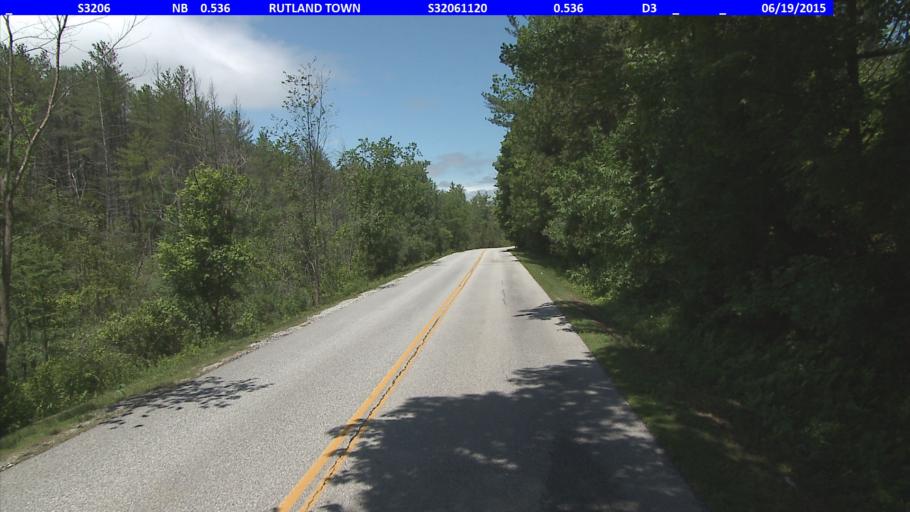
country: US
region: Vermont
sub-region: Rutland County
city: Rutland
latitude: 43.6372
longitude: -72.9909
